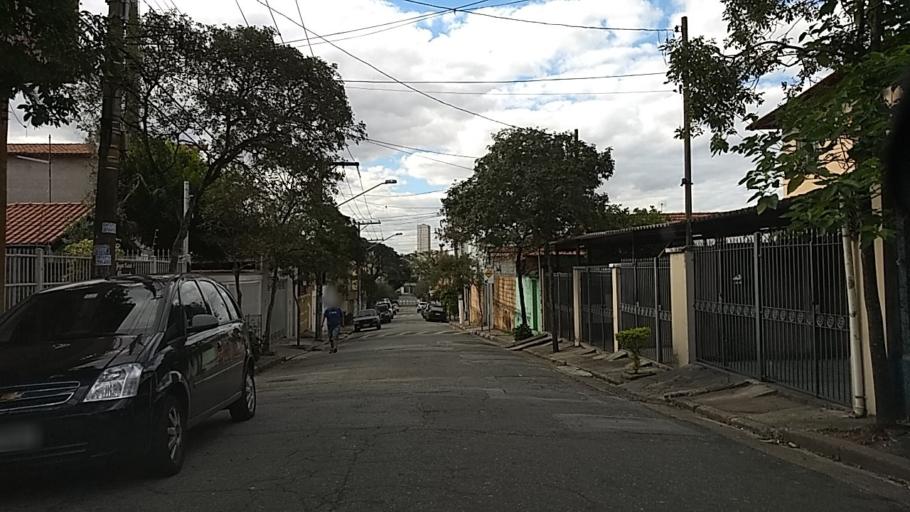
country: BR
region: Sao Paulo
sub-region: Guarulhos
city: Guarulhos
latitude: -23.4945
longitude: -46.5876
